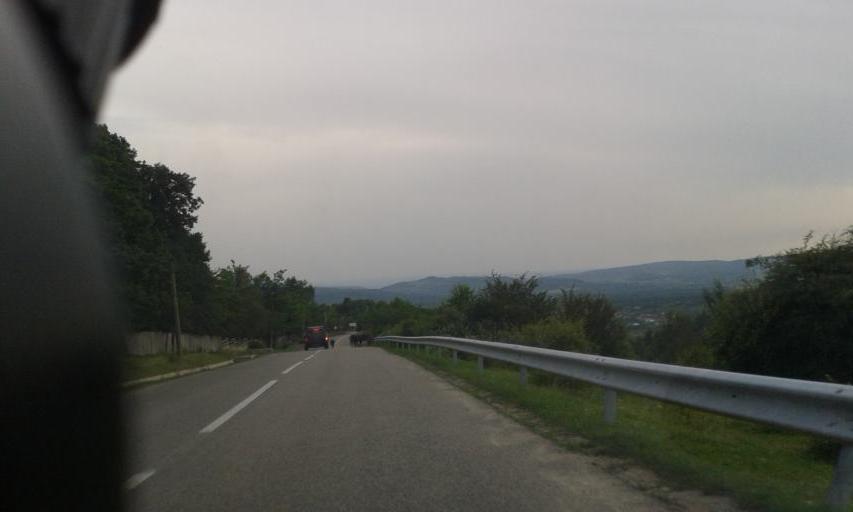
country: RO
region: Gorj
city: Novaci-Straini
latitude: 45.1927
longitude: 23.6853
